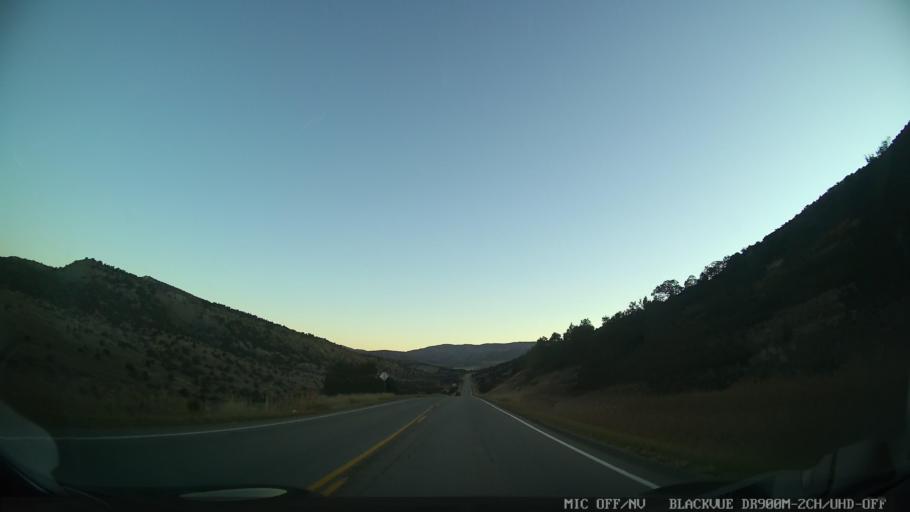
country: US
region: Colorado
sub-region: Eagle County
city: Edwards
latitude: 39.7102
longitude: -106.6826
